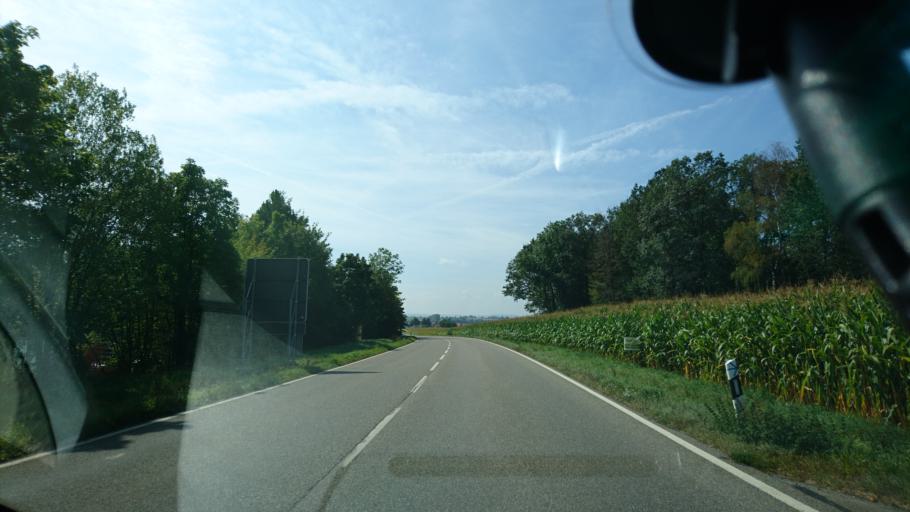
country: DE
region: Baden-Wuerttemberg
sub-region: Regierungsbezirk Stuttgart
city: Ilshofen
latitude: 49.1710
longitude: 9.9126
